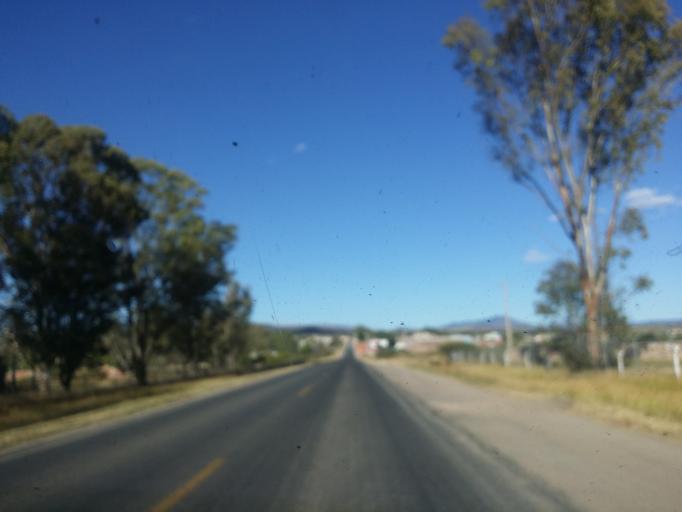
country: MX
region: Guanajuato
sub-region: Silao de la Victoria
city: El Refugio de los Sauces
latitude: 21.0356
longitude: -101.5252
